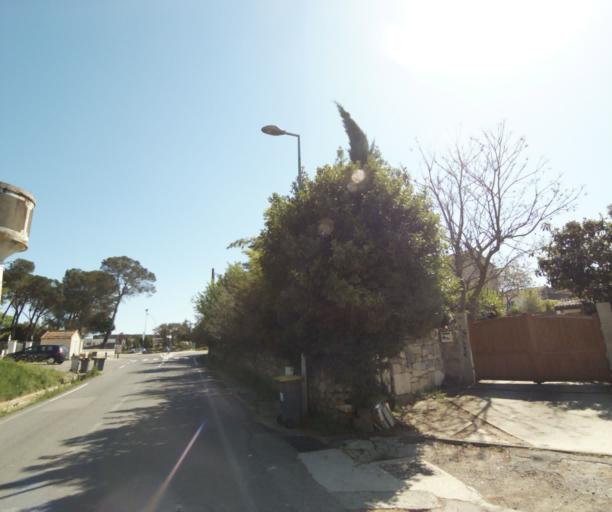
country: FR
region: Languedoc-Roussillon
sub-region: Departement de l'Herault
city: Saint-Drezery
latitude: 43.7348
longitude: 3.9794
